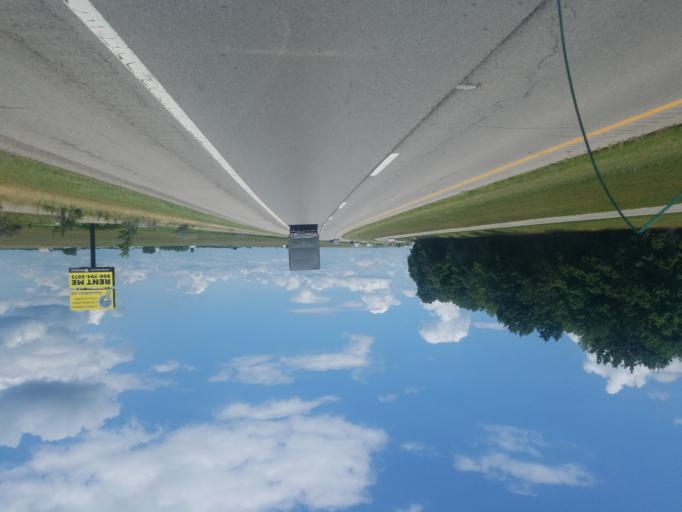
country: US
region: Ohio
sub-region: Wyandot County
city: Upper Sandusky
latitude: 40.7959
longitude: -83.2371
